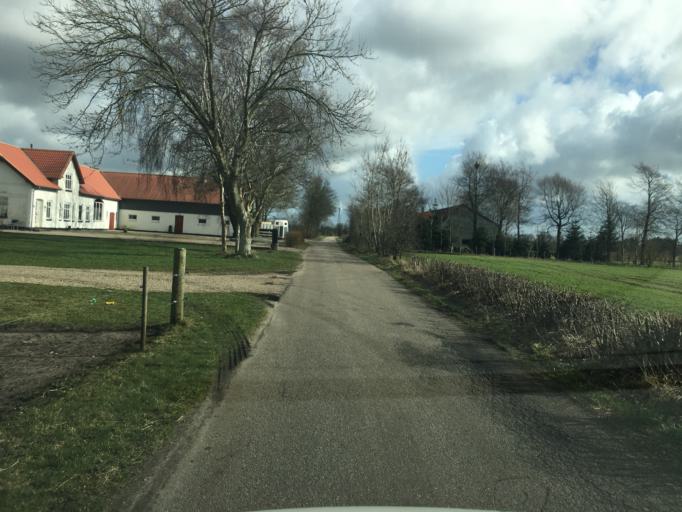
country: DK
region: South Denmark
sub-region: Aabenraa Kommune
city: Krusa
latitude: 54.9170
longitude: 9.3623
